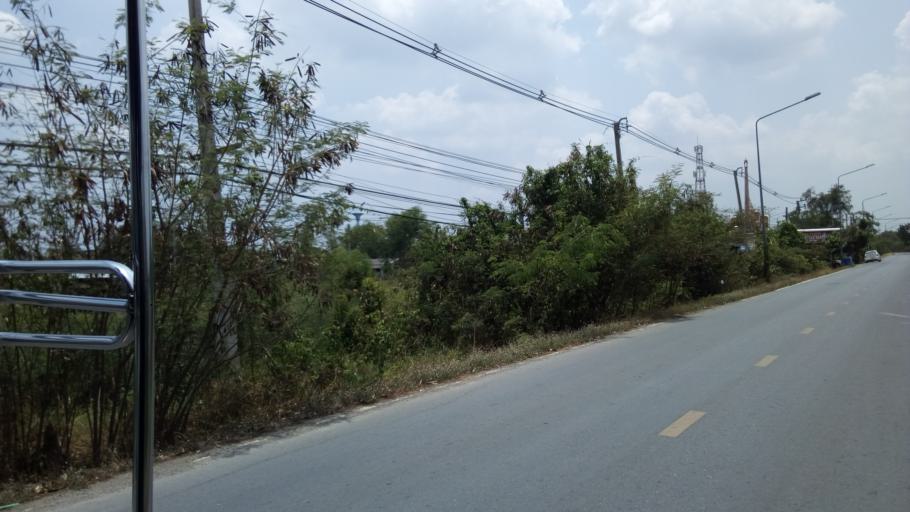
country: TH
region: Pathum Thani
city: Sam Khok
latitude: 14.0886
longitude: 100.5250
